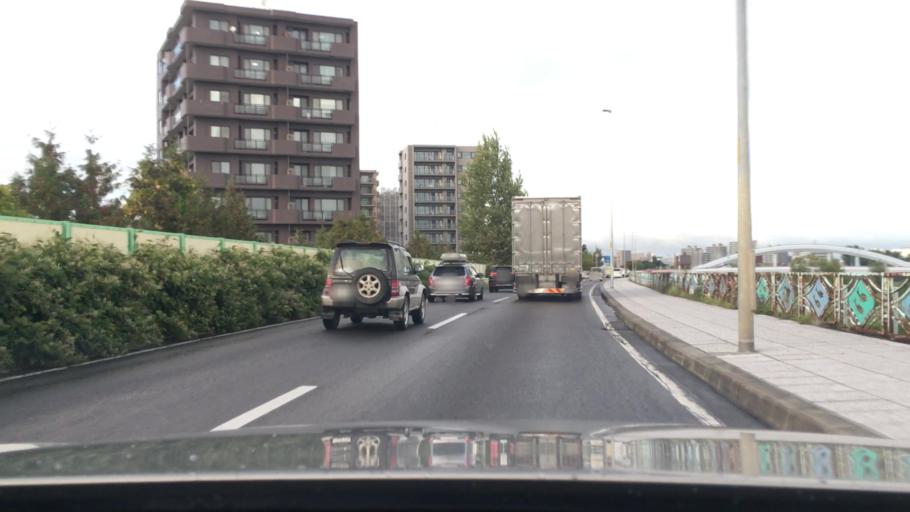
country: JP
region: Hokkaido
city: Sapporo
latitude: 43.0365
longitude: 141.3545
